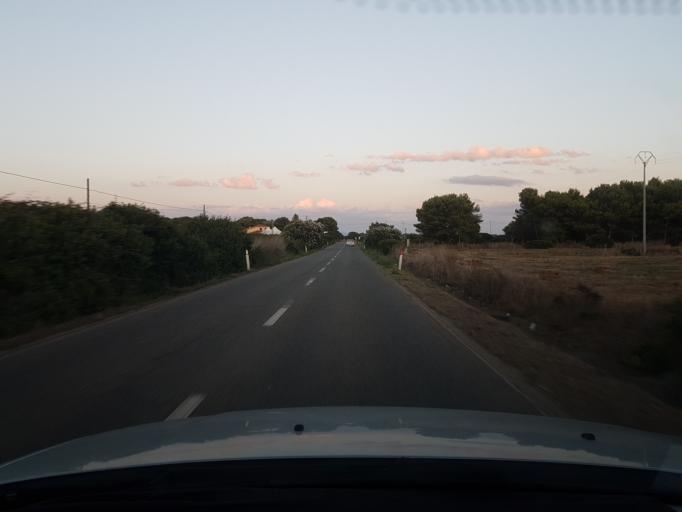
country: IT
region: Sardinia
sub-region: Provincia di Oristano
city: Riola Sardo
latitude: 40.0230
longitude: 8.4476
